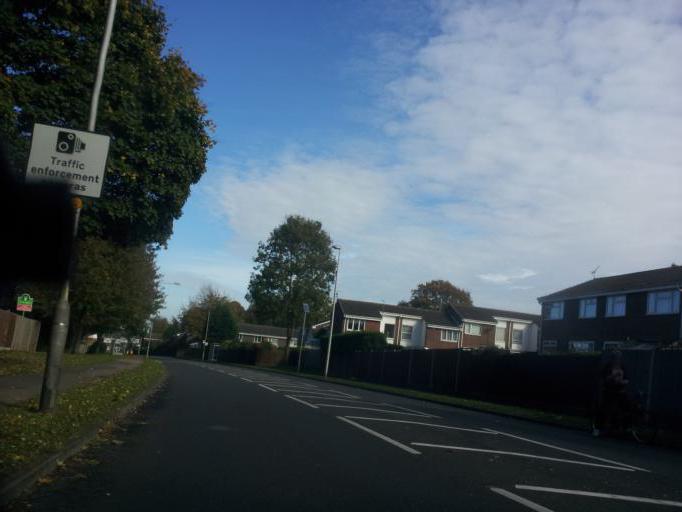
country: GB
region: England
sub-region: Kent
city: Rainham
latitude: 51.3425
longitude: 0.5969
